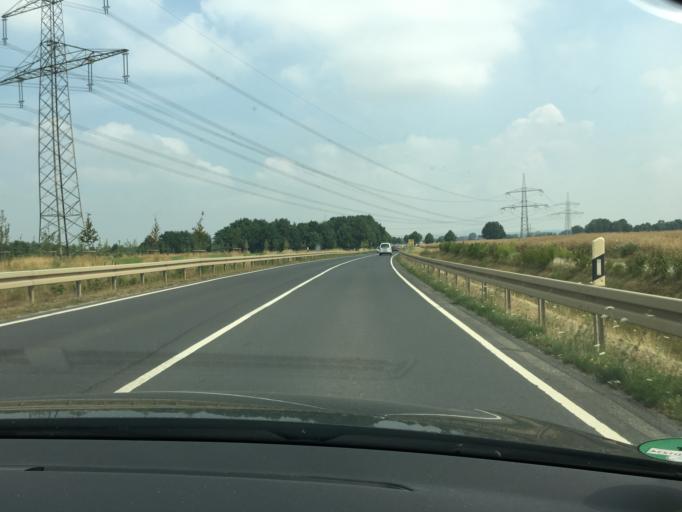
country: DE
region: North Rhine-Westphalia
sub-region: Regierungsbezirk Koln
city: Bergheim
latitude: 50.9089
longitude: 6.6162
